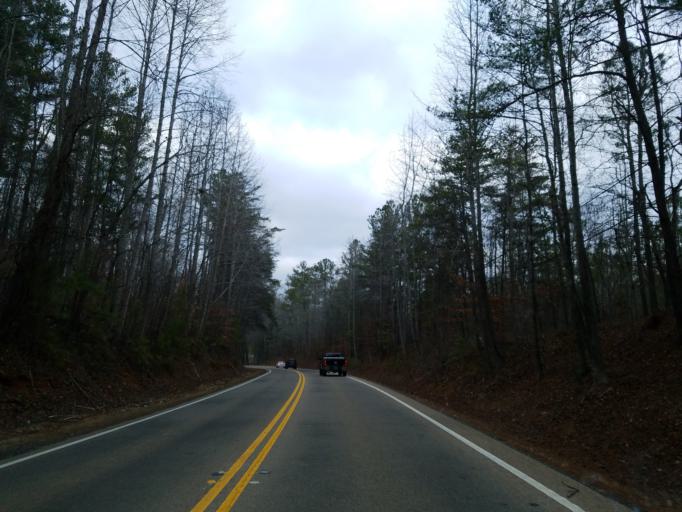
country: US
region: Georgia
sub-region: Cherokee County
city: Canton
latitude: 34.2960
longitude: -84.5178
